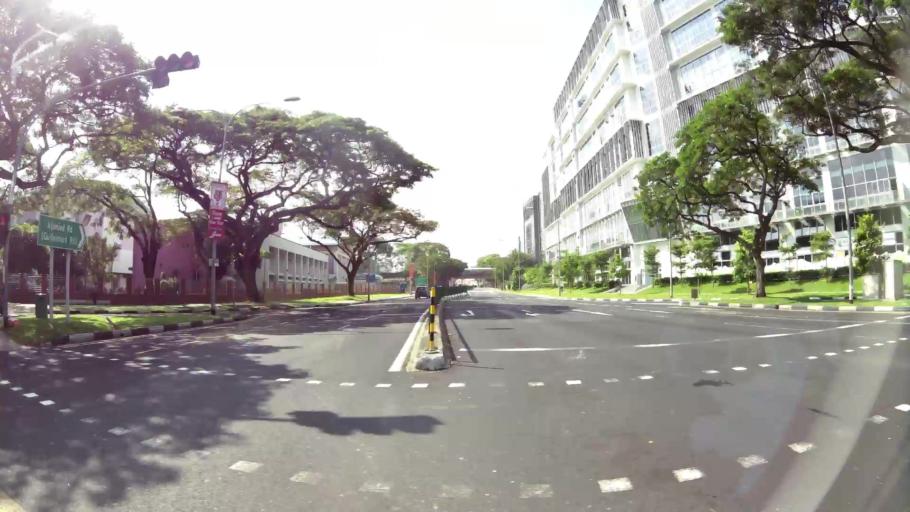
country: SG
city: Singapore
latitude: 1.3184
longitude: 103.8819
